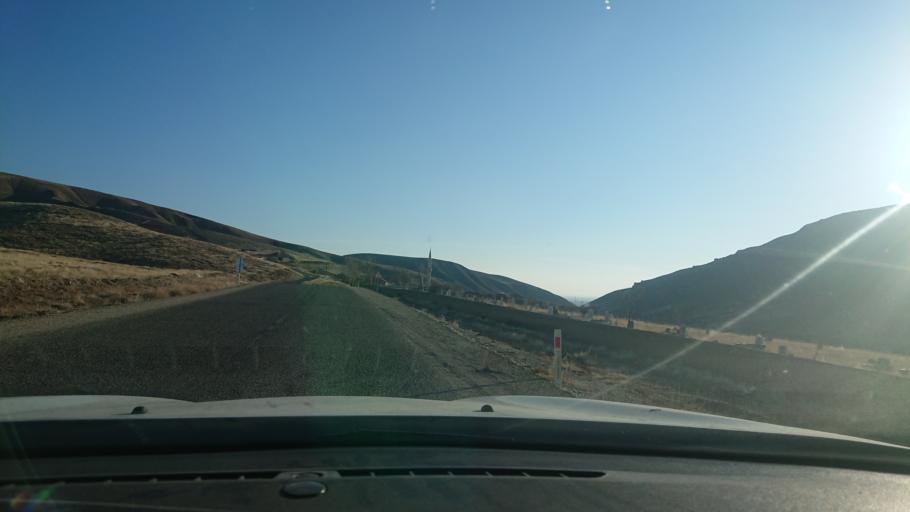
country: TR
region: Aksaray
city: Acipinar
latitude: 38.6950
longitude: 33.7485
